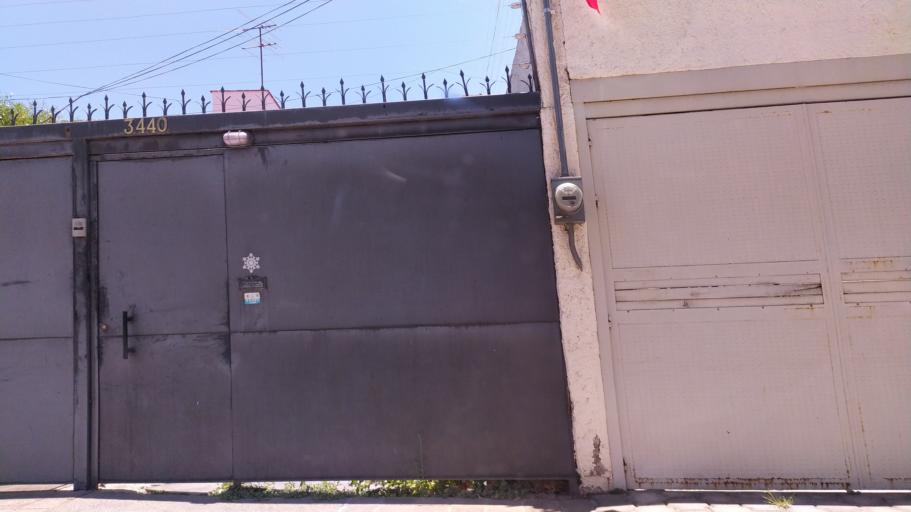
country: MX
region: Jalisco
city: Guadalajara
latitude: 20.6864
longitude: -103.3972
